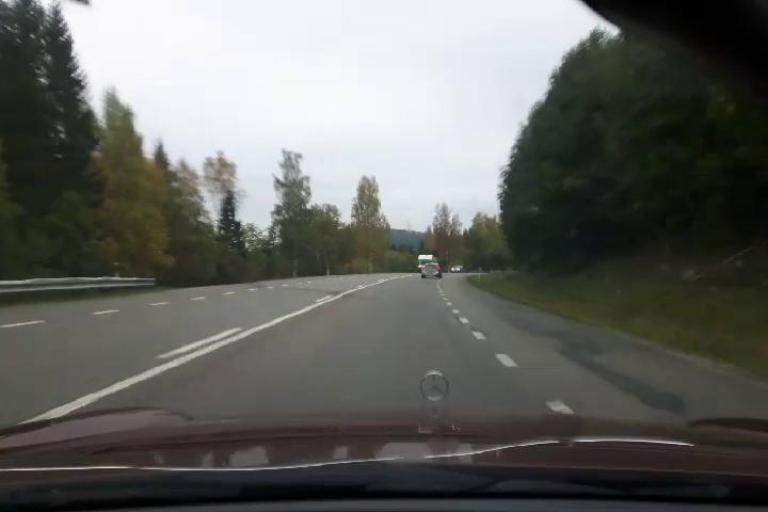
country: SE
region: Vaesternorrland
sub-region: Kramfors Kommun
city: Nordingra
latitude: 63.0328
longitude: 18.3214
